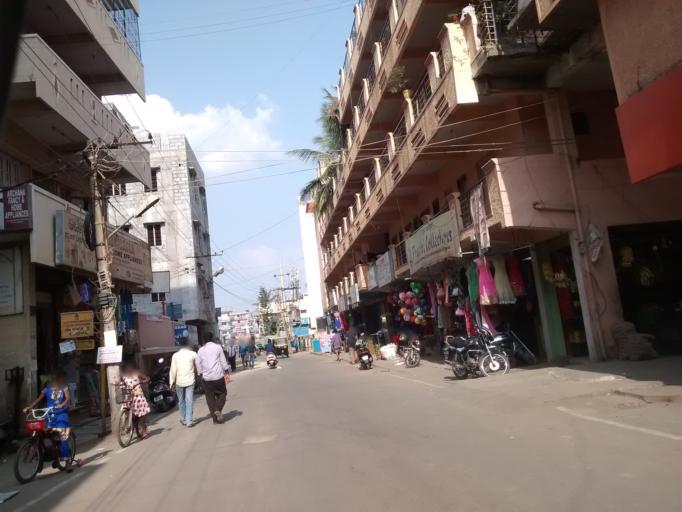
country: IN
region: Karnataka
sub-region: Bangalore Urban
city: Bangalore
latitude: 12.9646
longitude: 77.6735
